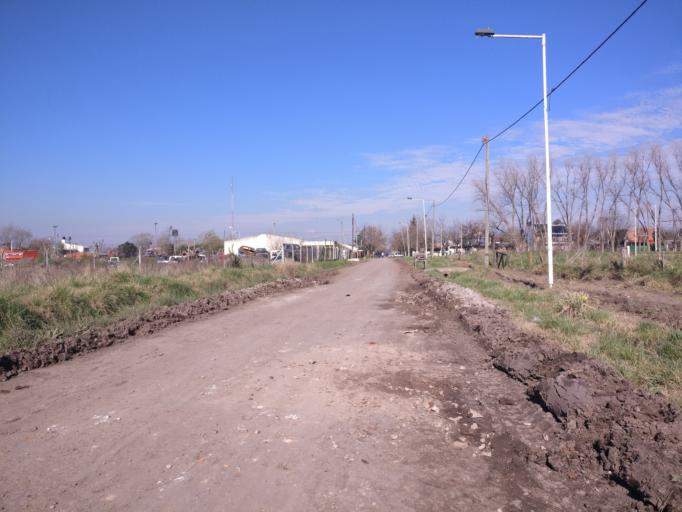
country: AR
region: Buenos Aires
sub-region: Partido de Ezeiza
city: Ezeiza
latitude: -34.9371
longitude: -58.6112
